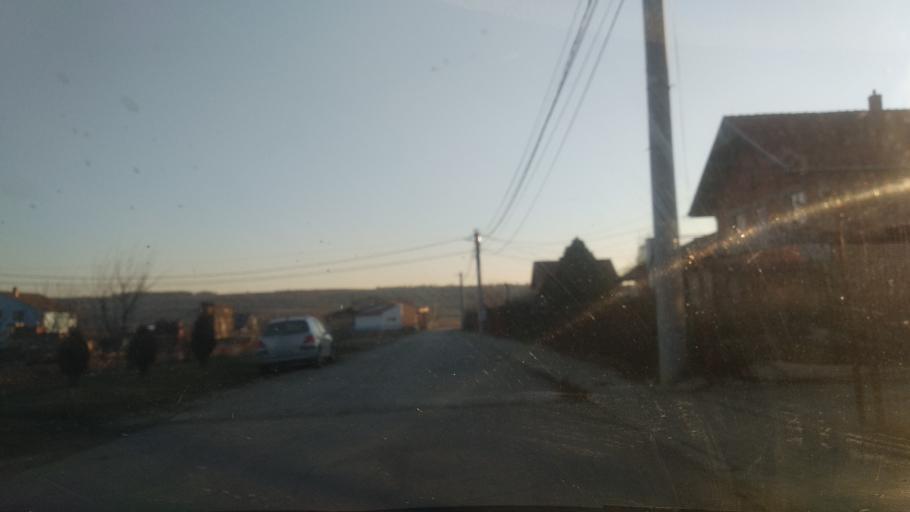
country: XK
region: Pristina
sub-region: Komuna e Prishtines
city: Pristina
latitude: 42.6030
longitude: 21.1825
